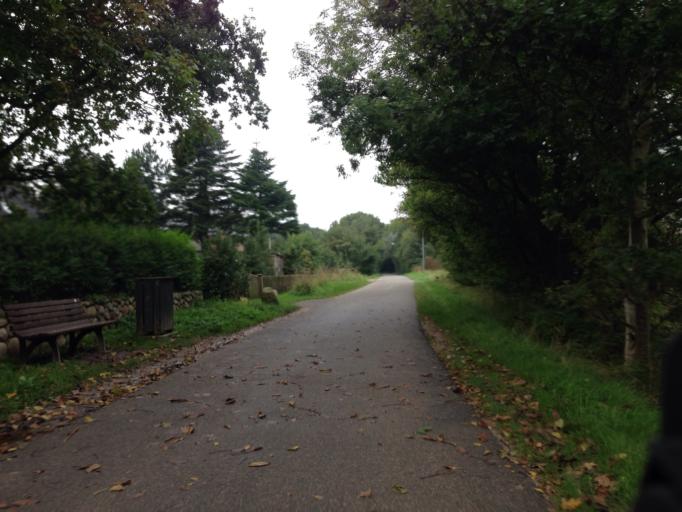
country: DE
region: Schleswig-Holstein
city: Wyk auf Fohr
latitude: 54.6939
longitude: 8.5645
